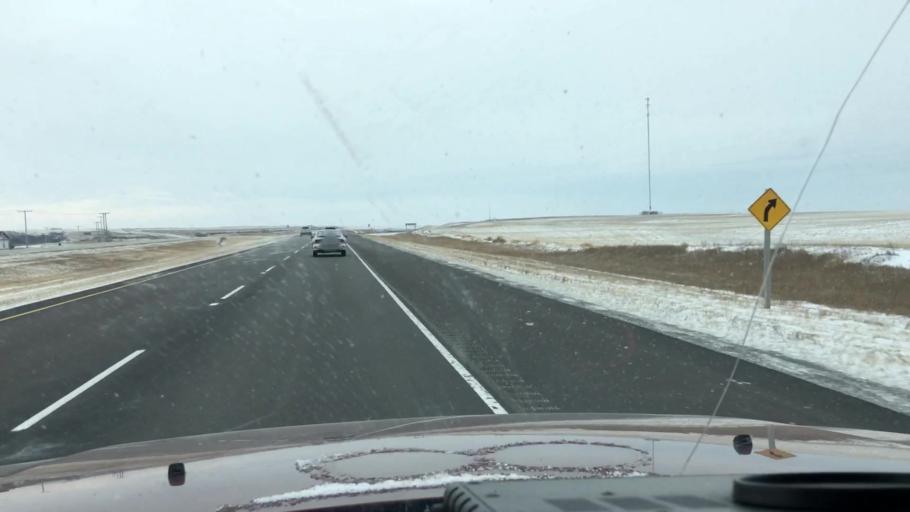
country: CA
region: Saskatchewan
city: Saskatoon
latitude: 51.7426
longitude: -106.4763
